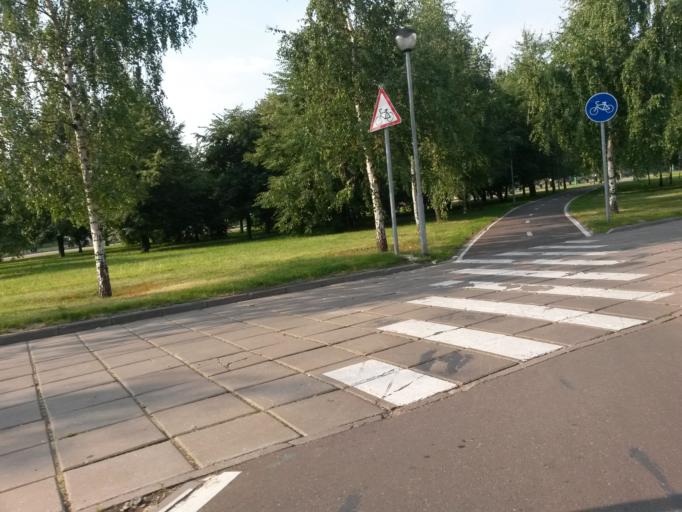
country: RU
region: Moscow
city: Brateyevo
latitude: 55.6445
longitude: 37.7571
